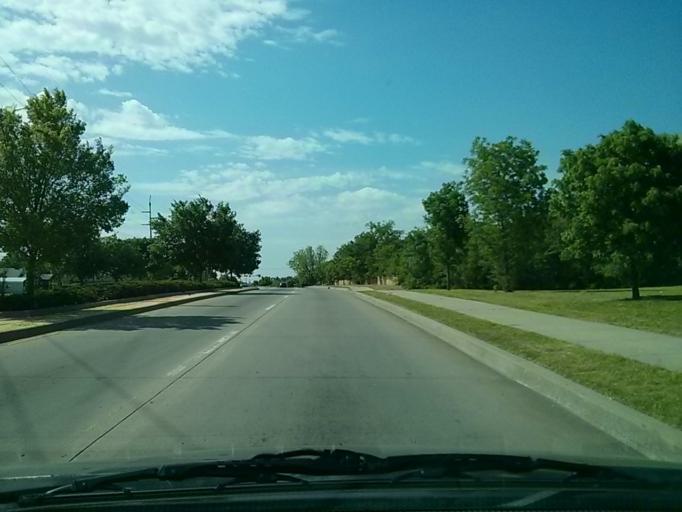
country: US
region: Oklahoma
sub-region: Tulsa County
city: Tulsa
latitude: 36.1959
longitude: -95.9757
